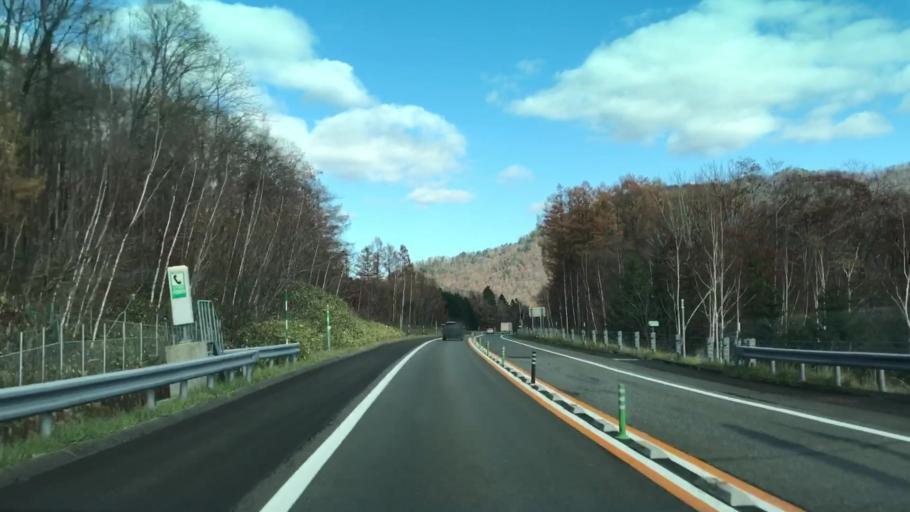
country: JP
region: Hokkaido
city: Chitose
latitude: 42.9137
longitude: 142.0197
